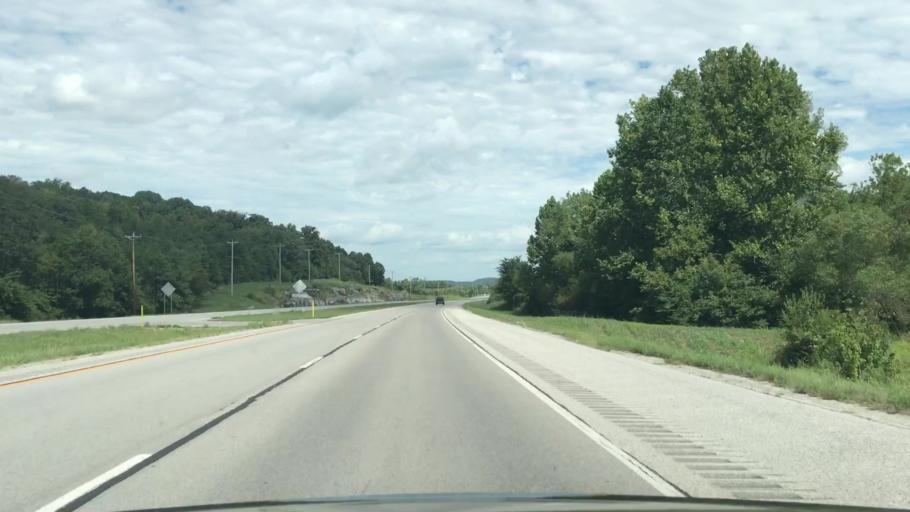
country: US
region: Kentucky
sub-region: Logan County
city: Russellville
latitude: 36.8460
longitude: -86.8638
